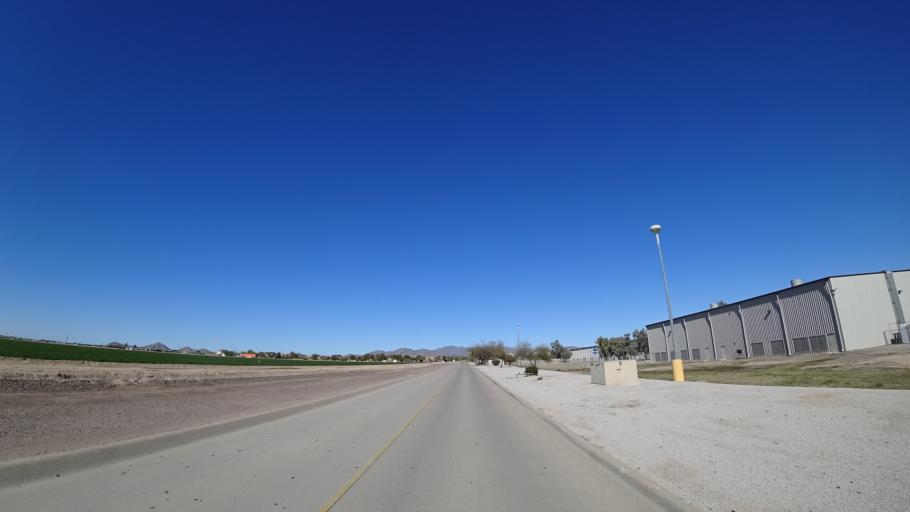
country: US
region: Arizona
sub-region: Maricopa County
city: Buckeye
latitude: 33.3887
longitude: -112.5649
